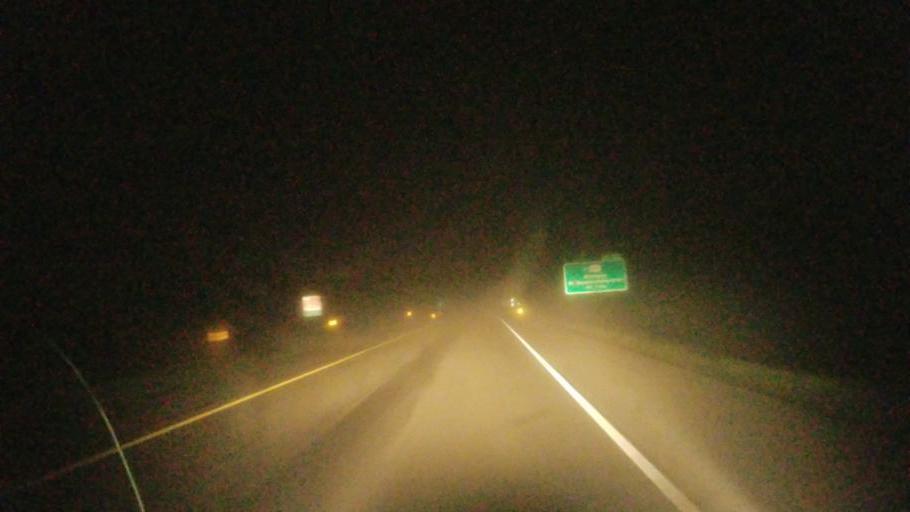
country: US
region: New York
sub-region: Cattaraugus County
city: Allegany
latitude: 42.0974
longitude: -78.5298
